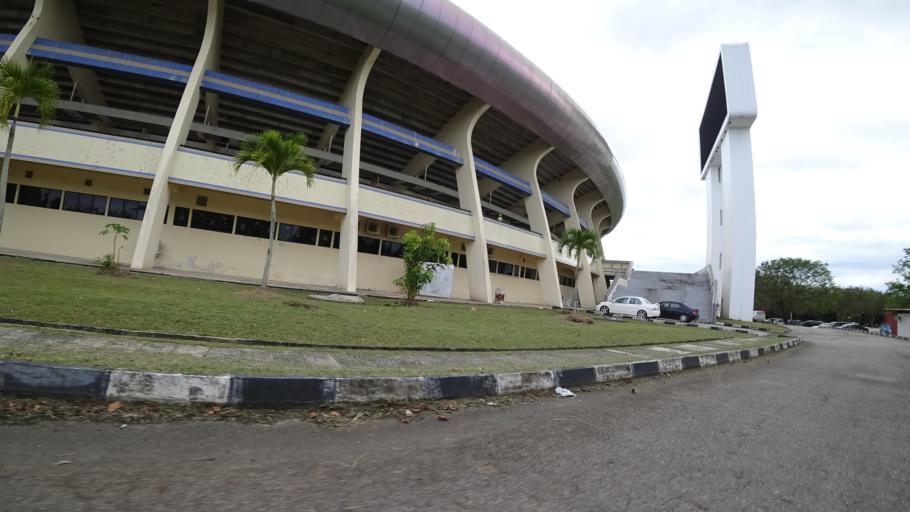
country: BN
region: Brunei and Muara
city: Bandar Seri Begawan
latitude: 4.9302
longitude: 114.9457
